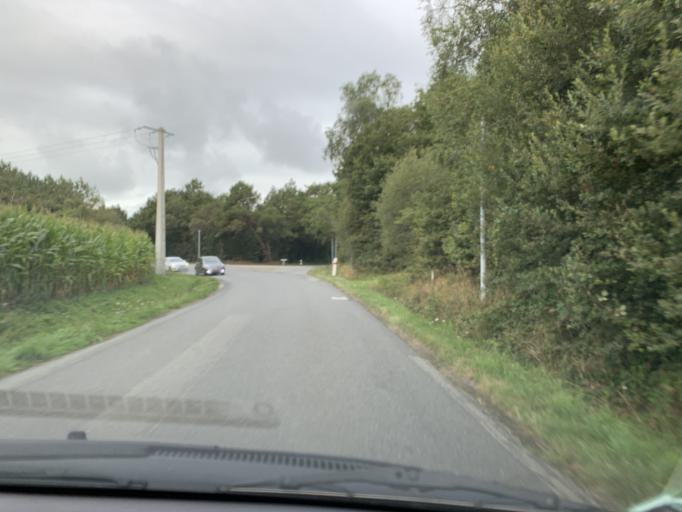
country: FR
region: Pays de la Loire
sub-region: Departement de la Loire-Atlantique
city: Asserac
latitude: 47.4699
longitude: -2.3983
